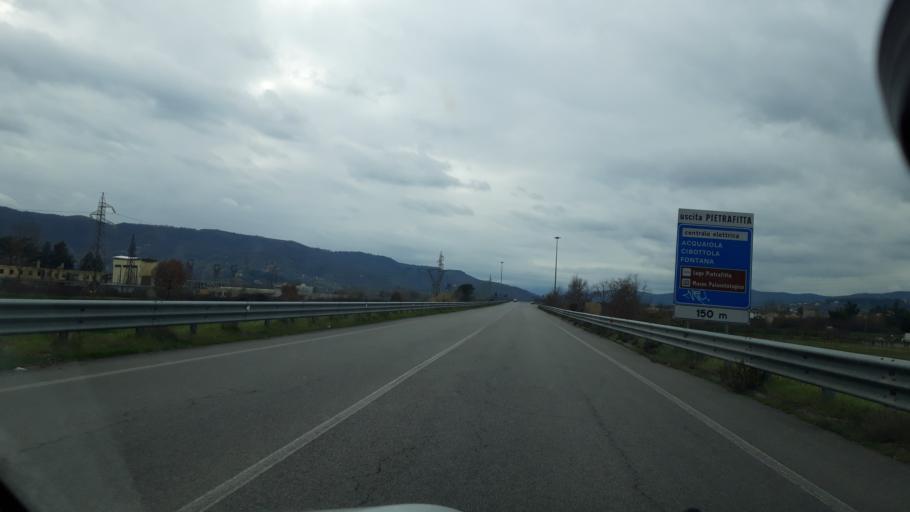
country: IT
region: Umbria
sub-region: Provincia di Perugia
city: Fontignano
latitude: 43.0070
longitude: 12.1838
